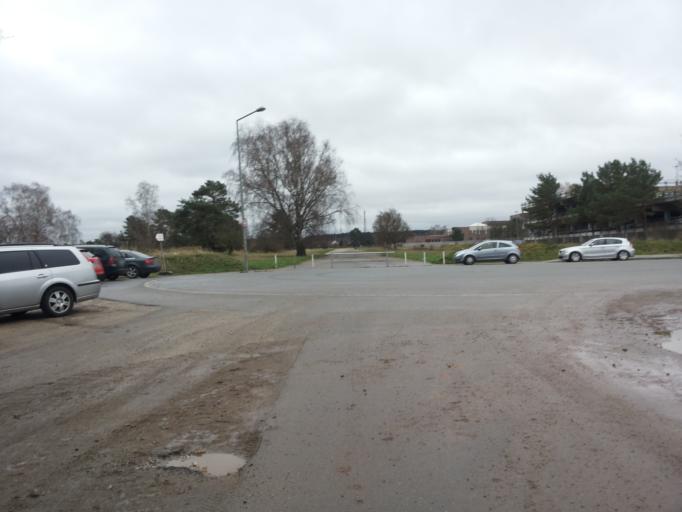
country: DE
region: Bavaria
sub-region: Regierungsbezirk Mittelfranken
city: Wendelstein
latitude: 49.4033
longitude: 11.1625
